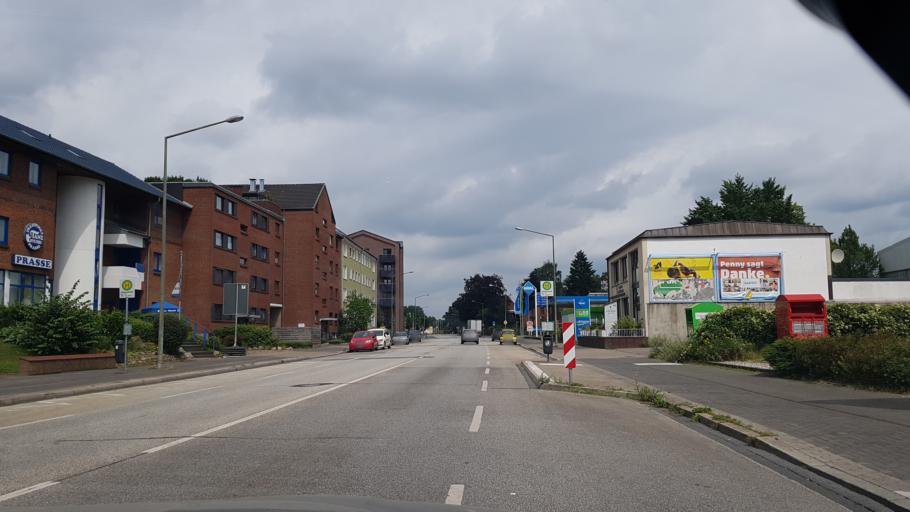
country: DE
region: Schleswig-Holstein
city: Neumunster
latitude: 54.0814
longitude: 9.9793
